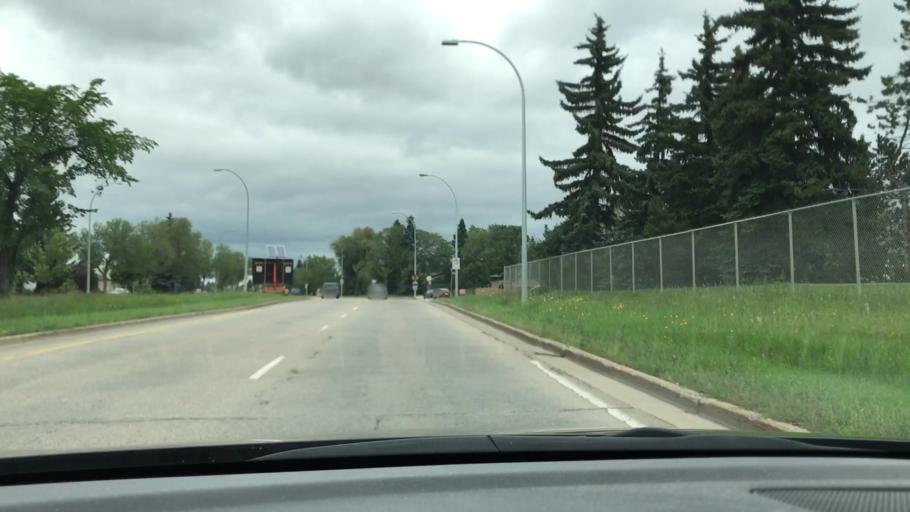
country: CA
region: Alberta
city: Edmonton
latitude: 53.5139
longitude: -113.5783
